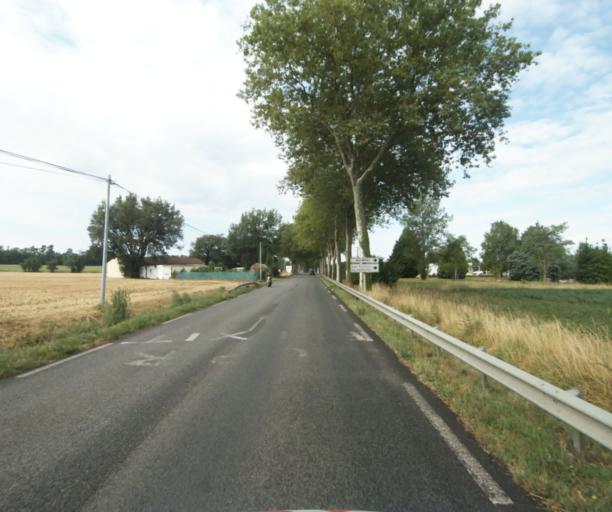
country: FR
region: Midi-Pyrenees
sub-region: Departement de la Haute-Garonne
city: Revel
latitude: 43.4483
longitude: 1.9651
